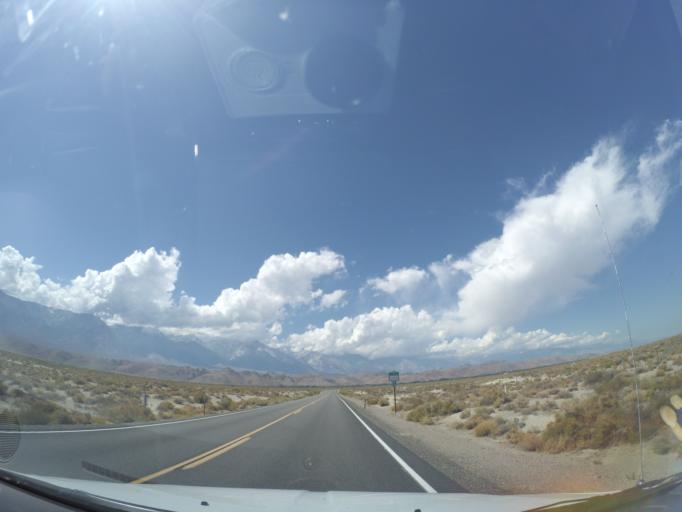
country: US
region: California
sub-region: Inyo County
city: Lone Pine
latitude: 36.5761
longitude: -118.0224
